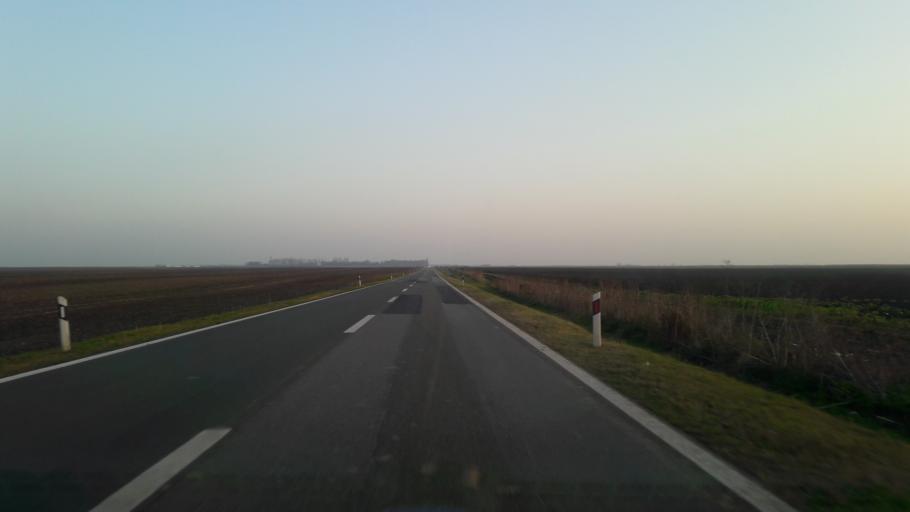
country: HR
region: Osjecko-Baranjska
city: Tenja
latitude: 45.5095
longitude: 18.7931
